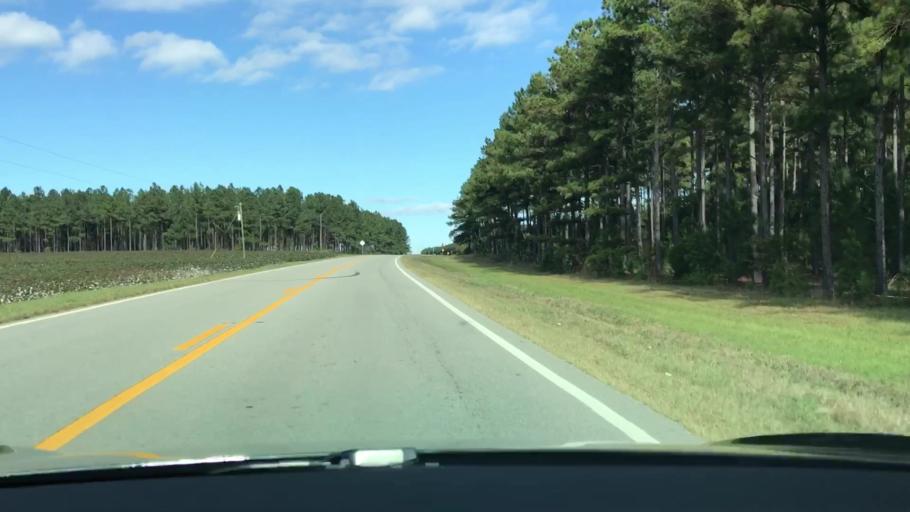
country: US
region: Georgia
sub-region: Glascock County
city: Gibson
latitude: 33.2779
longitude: -82.5027
